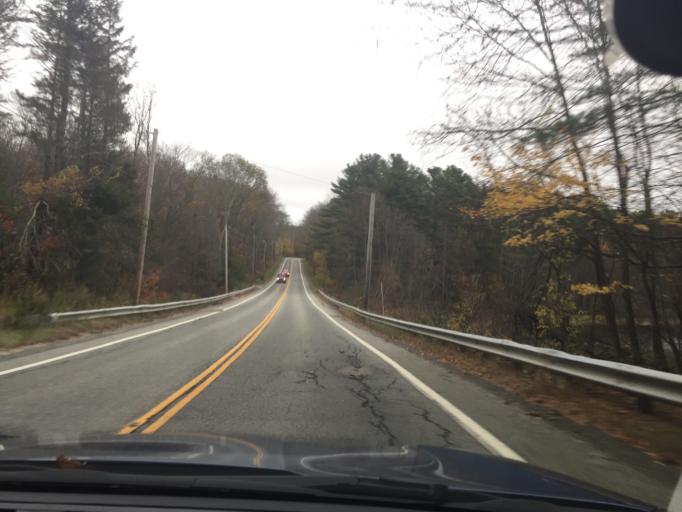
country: US
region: Rhode Island
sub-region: Providence County
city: North Scituate
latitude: 41.7927
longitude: -71.6464
